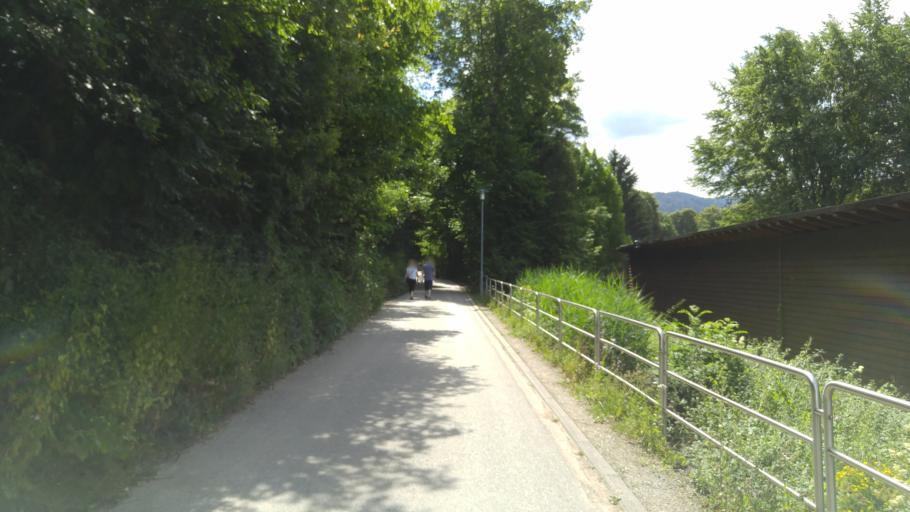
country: DE
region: Baden-Wuerttemberg
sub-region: Freiburg Region
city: Sulzburg
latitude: 47.8734
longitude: 7.7362
